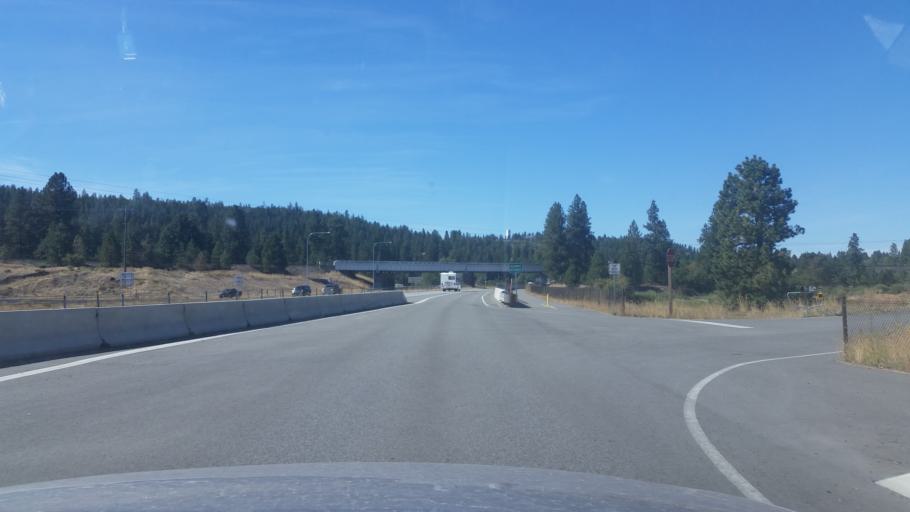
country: US
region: Washington
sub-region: Spokane County
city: Spokane
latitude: 47.6208
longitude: -117.4342
